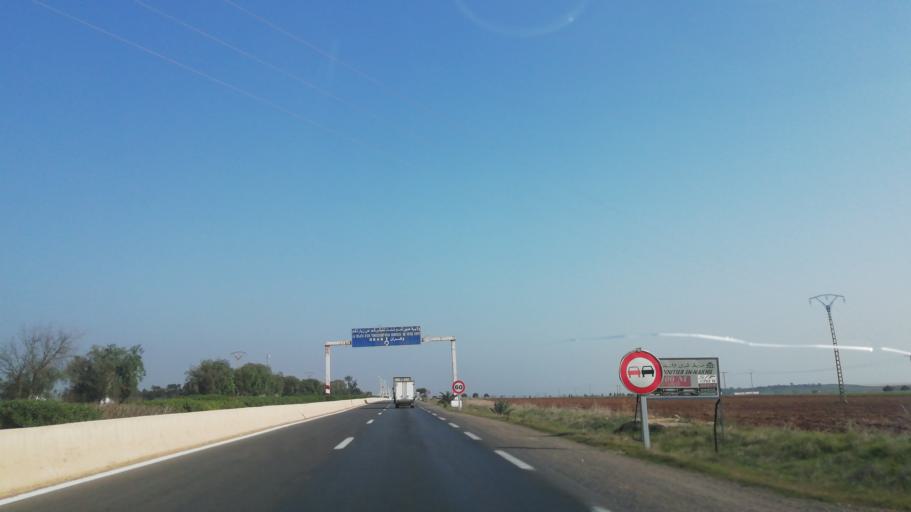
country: DZ
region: Ain Temouchent
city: El Amria
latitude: 35.5441
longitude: -0.9681
